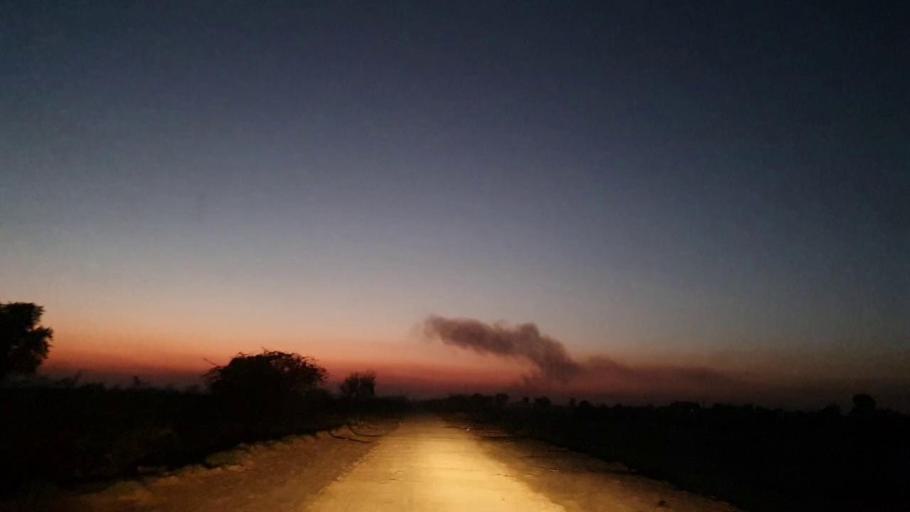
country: PK
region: Sindh
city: Nawabshah
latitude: 26.3183
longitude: 68.3754
